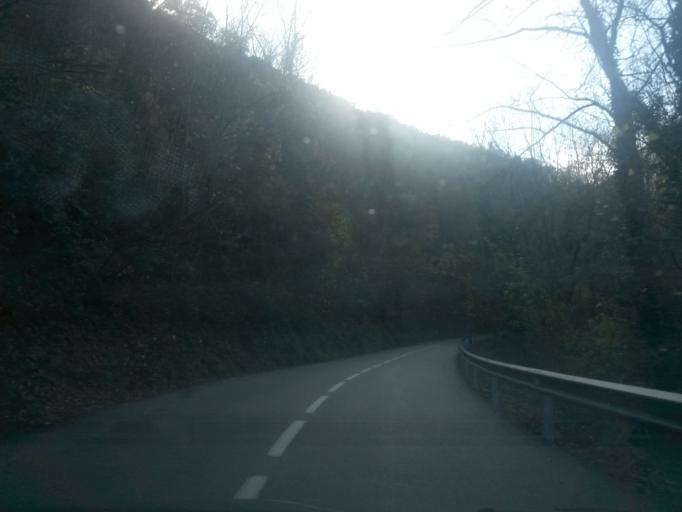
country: ES
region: Catalonia
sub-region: Provincia de Girona
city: Susqueda
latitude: 41.9361
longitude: 2.5200
